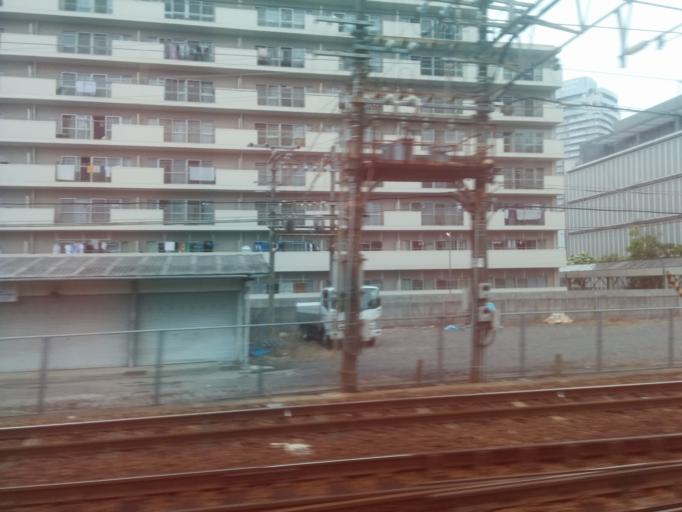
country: JP
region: Shiga Prefecture
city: Kusatsu
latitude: 35.0210
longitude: 135.9601
